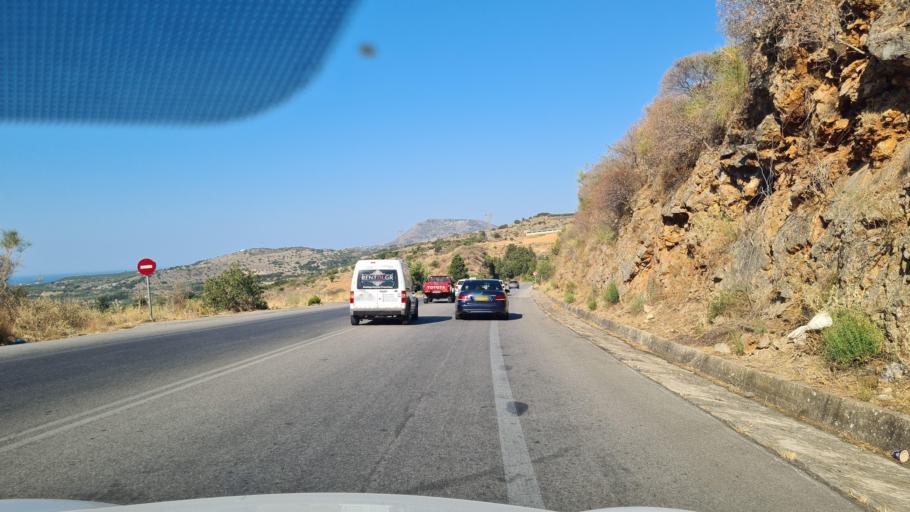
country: GR
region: Crete
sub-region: Nomos Chanias
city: Kalivai
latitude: 35.4164
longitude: 24.1506
